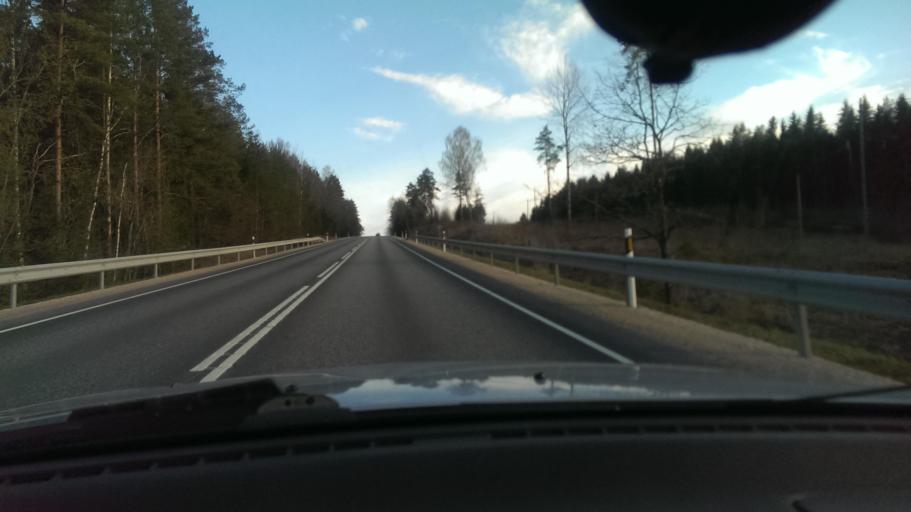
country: EE
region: Vorumaa
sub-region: Antsla vald
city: Vana-Antsla
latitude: 58.0015
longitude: 26.7612
